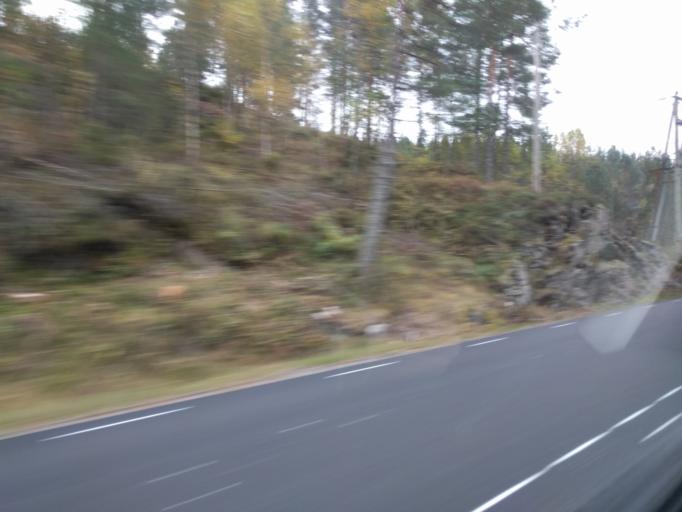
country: NO
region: Aust-Agder
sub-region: Iveland
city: Birketveit
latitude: 58.4368
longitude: 7.7867
